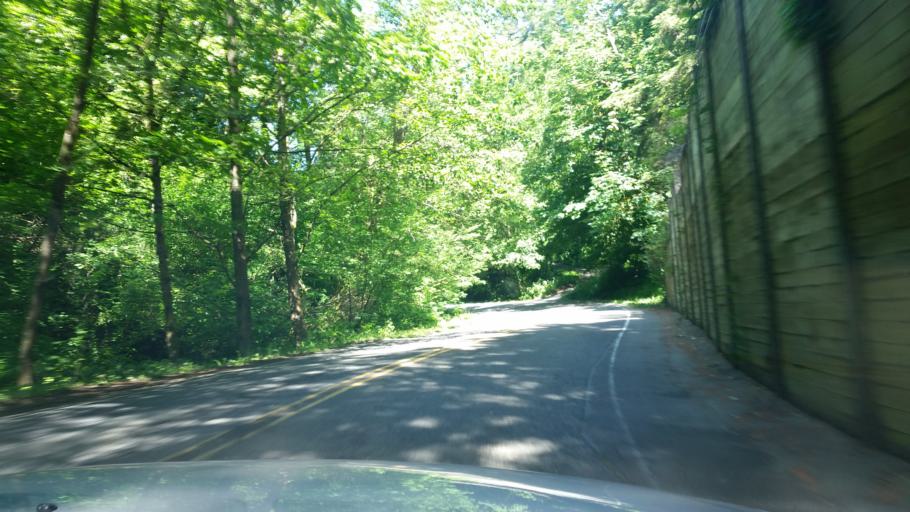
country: US
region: Washington
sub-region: King County
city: Lake Forest Park
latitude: 47.7624
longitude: -122.3006
